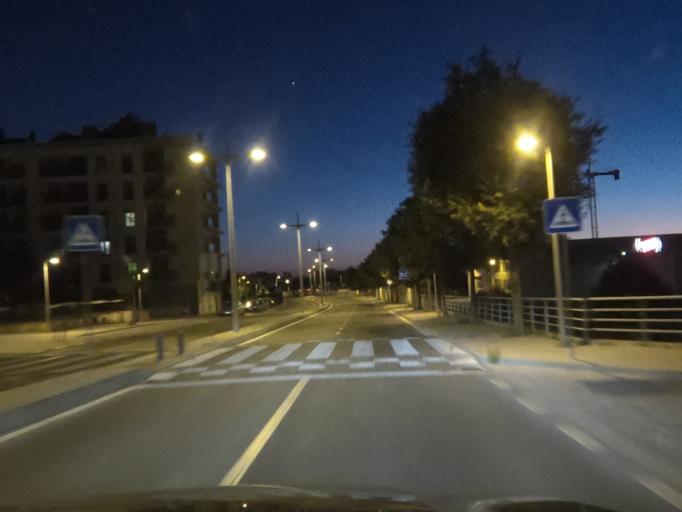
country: PT
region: Faro
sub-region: Loule
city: Loule
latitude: 37.1380
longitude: -7.9990
